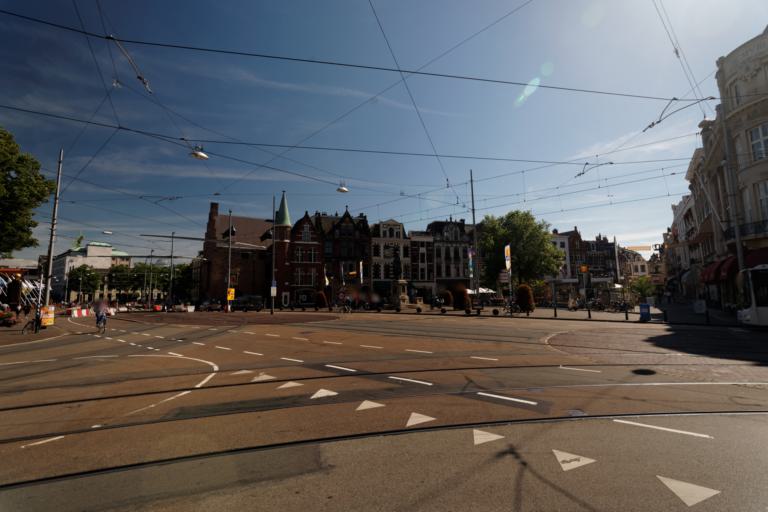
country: NL
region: South Holland
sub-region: Gemeente Den Haag
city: The Hague
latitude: 52.0803
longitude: 4.3101
